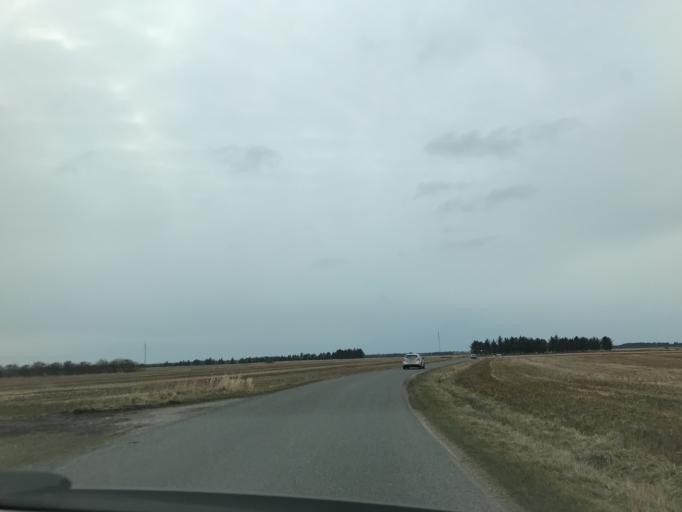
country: DK
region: South Denmark
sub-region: Varde Kommune
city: Oksbol
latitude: 55.8173
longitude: 8.2836
